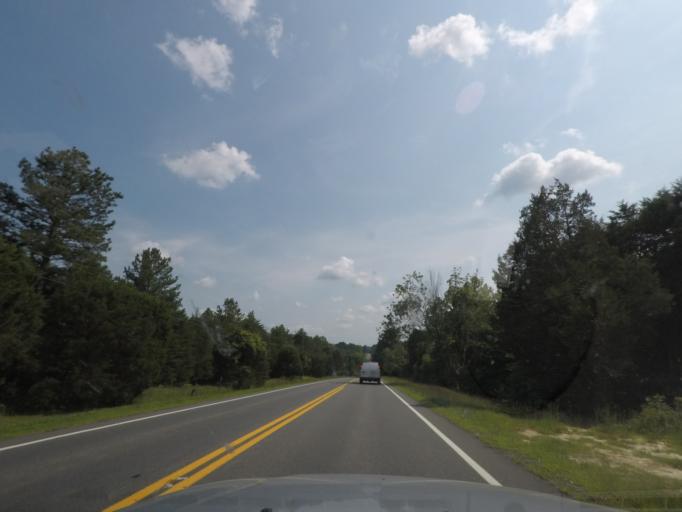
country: US
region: Virginia
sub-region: Fluvanna County
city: Palmyra
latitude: 37.8449
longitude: -78.2723
